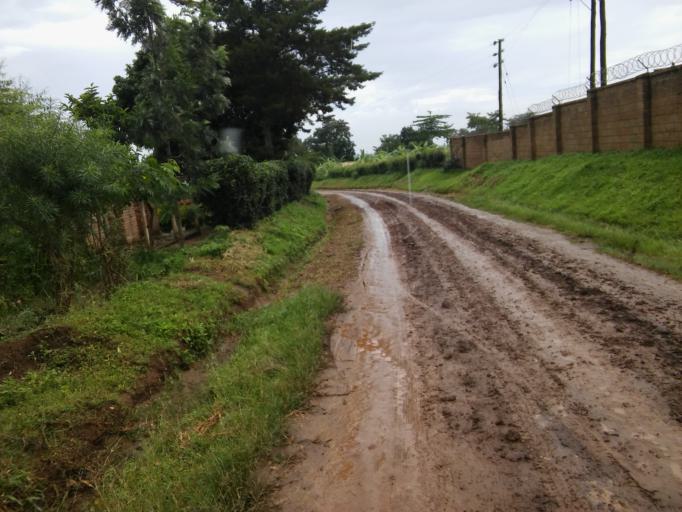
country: UG
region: Eastern Region
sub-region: Mbale District
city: Mbale
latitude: 1.0369
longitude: 34.2039
